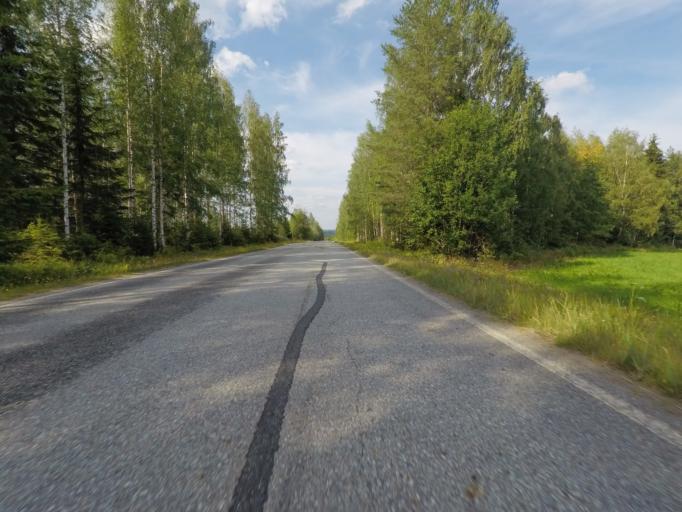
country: FI
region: Southern Savonia
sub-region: Savonlinna
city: Sulkava
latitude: 61.7079
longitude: 28.2105
